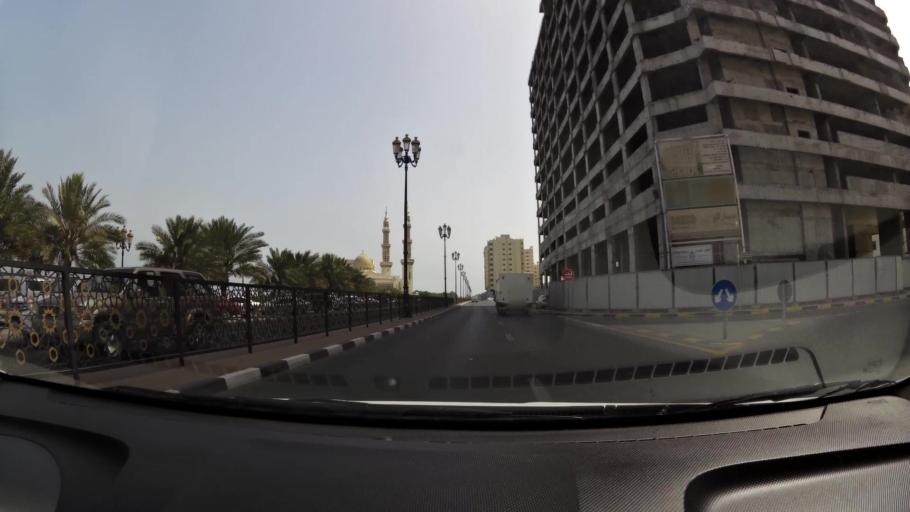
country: AE
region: Ash Shariqah
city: Sharjah
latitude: 25.3664
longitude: 55.3899
